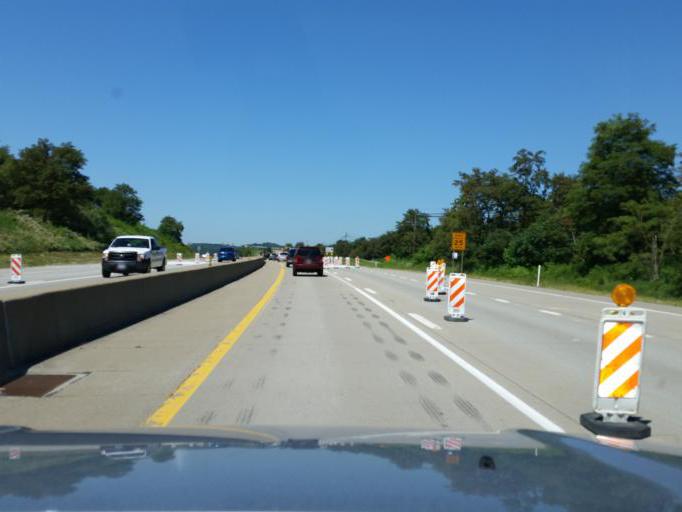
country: US
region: Pennsylvania
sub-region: Westmoreland County
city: Delmont
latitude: 40.3981
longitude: -79.4633
